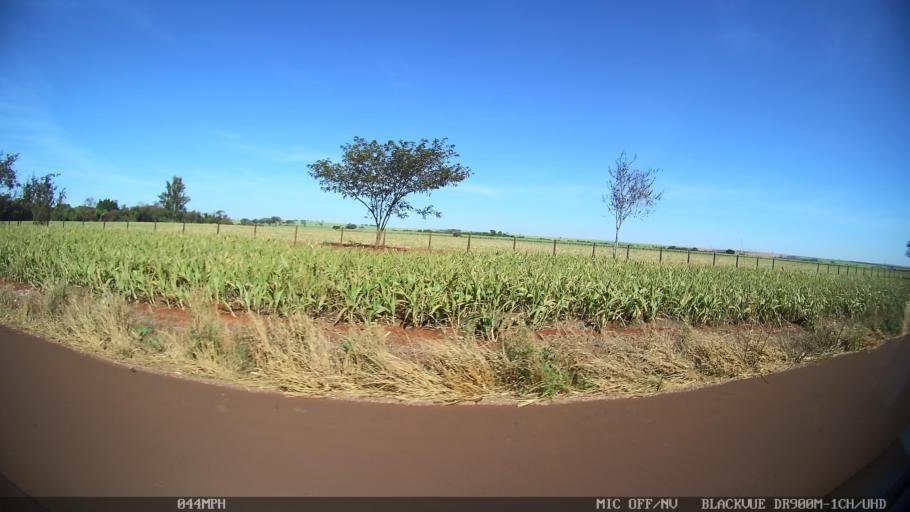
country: BR
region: Sao Paulo
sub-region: Ipua
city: Ipua
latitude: -20.5046
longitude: -47.9351
